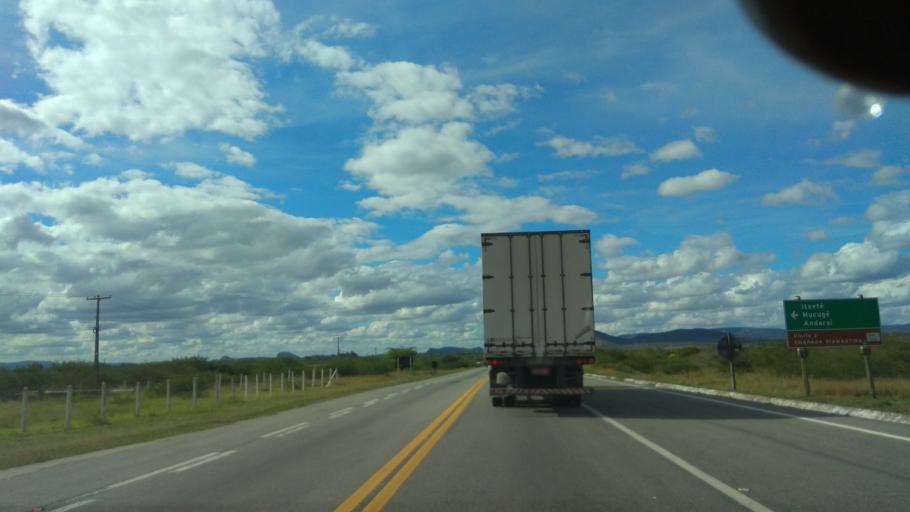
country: BR
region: Bahia
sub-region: Amargosa
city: Amargosa
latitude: -12.8500
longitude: -39.8435
